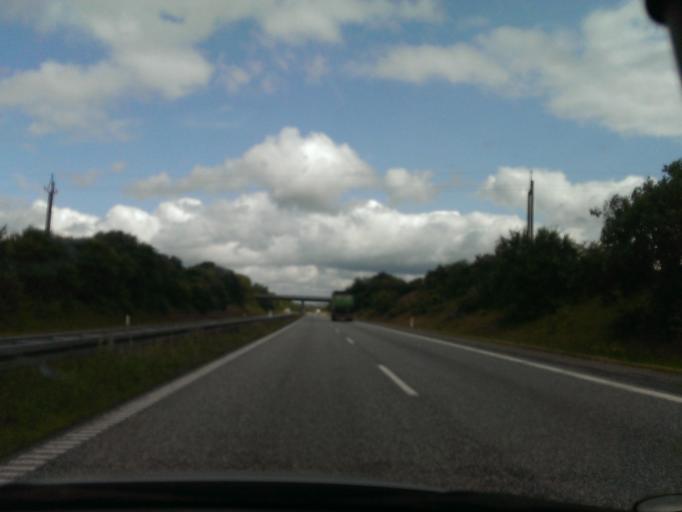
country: DK
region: North Denmark
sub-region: Mariagerfjord Kommune
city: Hobro
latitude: 56.6827
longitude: 9.7319
